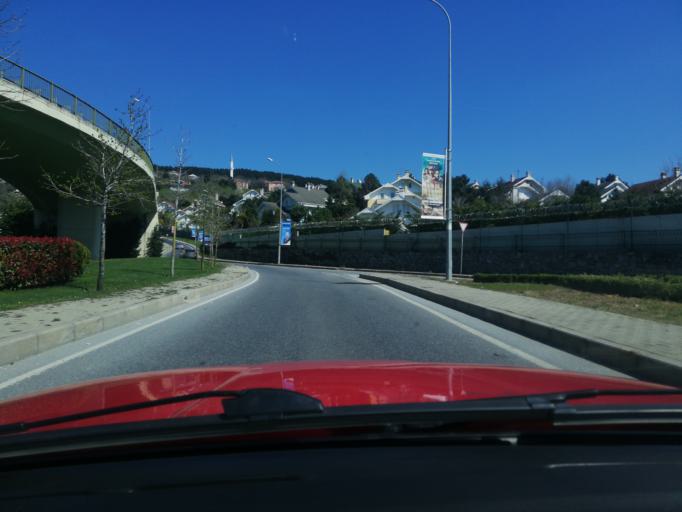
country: TR
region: Istanbul
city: Mahmut Sevket Pasa
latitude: 41.1211
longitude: 29.1295
